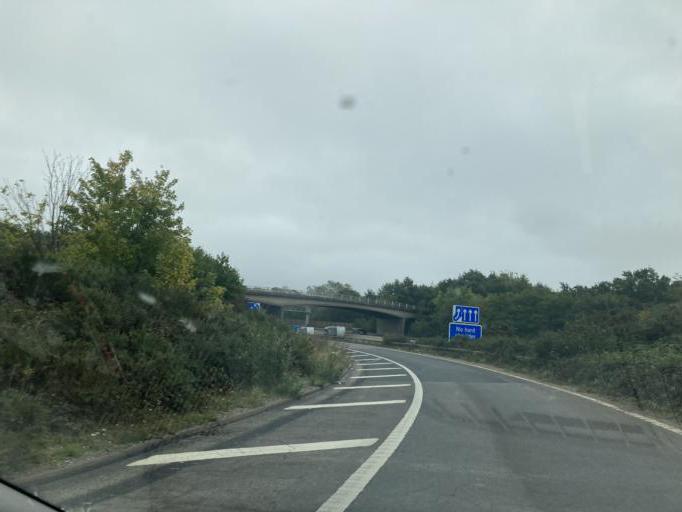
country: GB
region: England
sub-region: Hampshire
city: Farnborough
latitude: 51.3032
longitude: -0.7946
